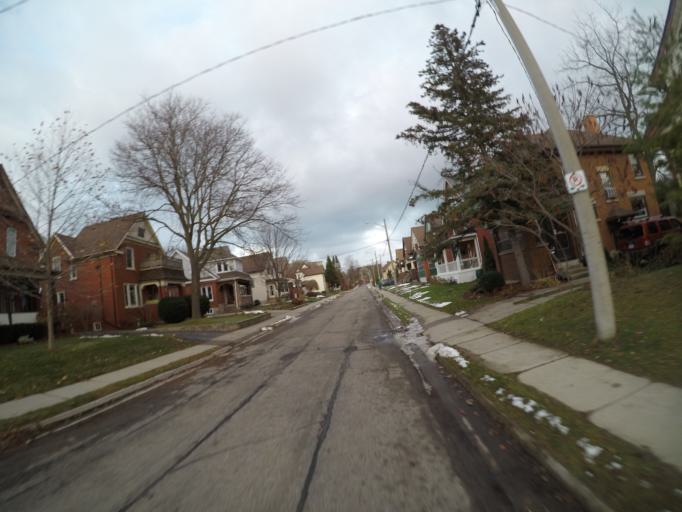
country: CA
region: Ontario
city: Waterloo
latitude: 43.4594
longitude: -80.4957
